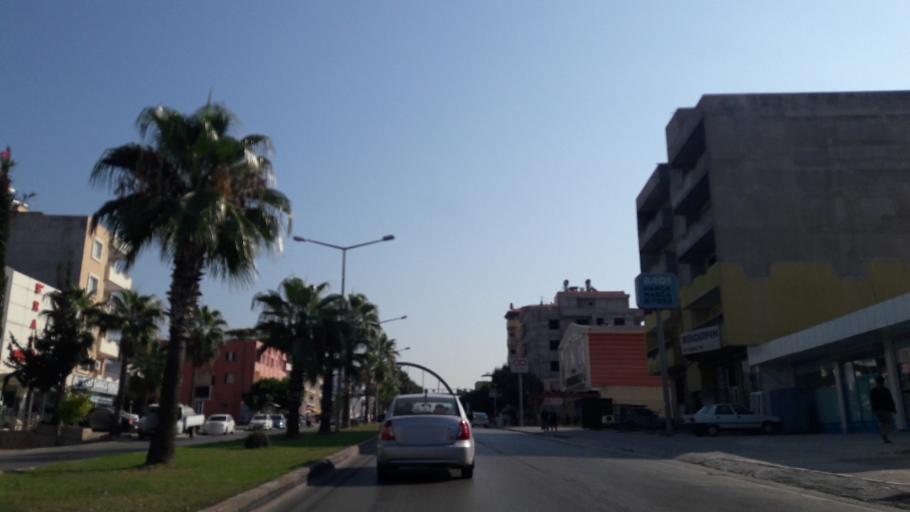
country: TR
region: Adana
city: Yuregir
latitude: 37.0373
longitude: 35.4211
